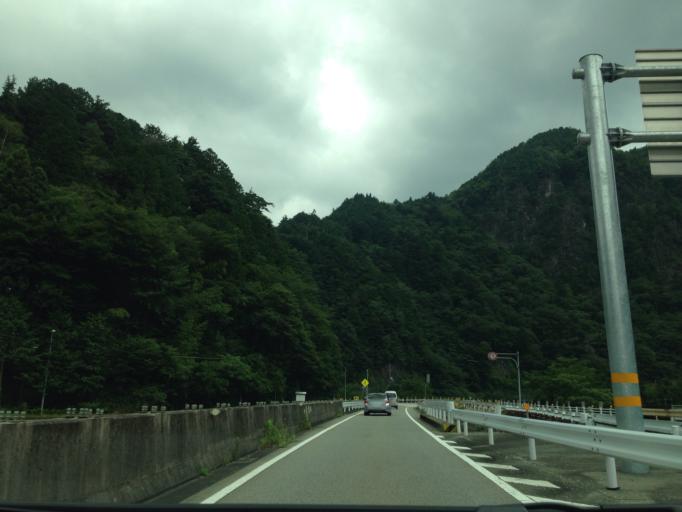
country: JP
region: Gifu
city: Gujo
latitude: 35.7477
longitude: 137.2099
